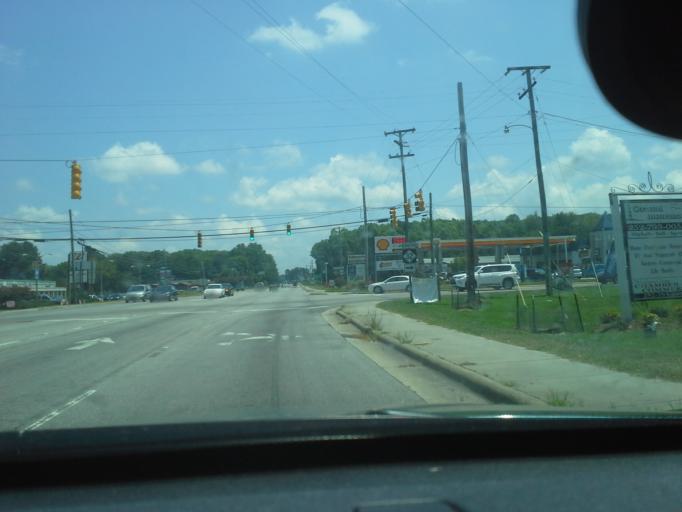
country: US
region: North Carolina
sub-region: Washington County
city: Plymouth
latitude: 35.8582
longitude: -76.7459
